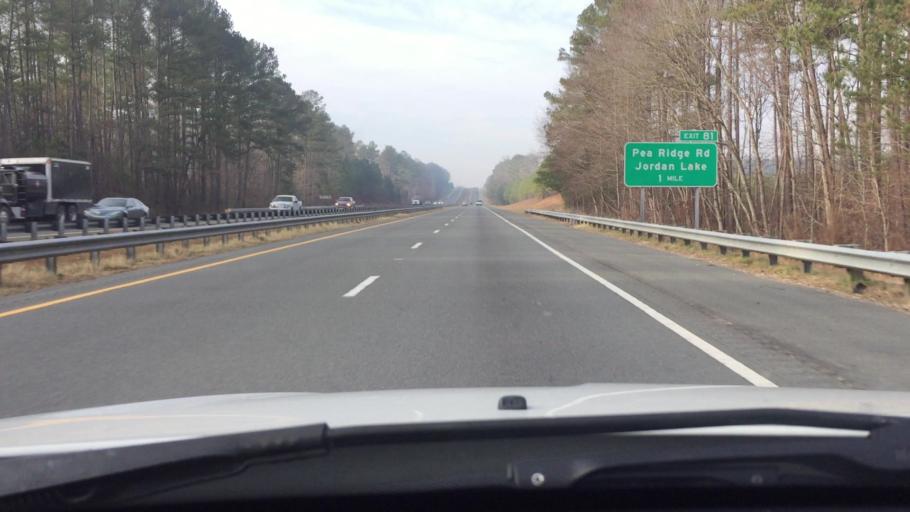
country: US
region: North Carolina
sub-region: Chatham County
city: Pittsboro
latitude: 35.6400
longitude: -79.0337
